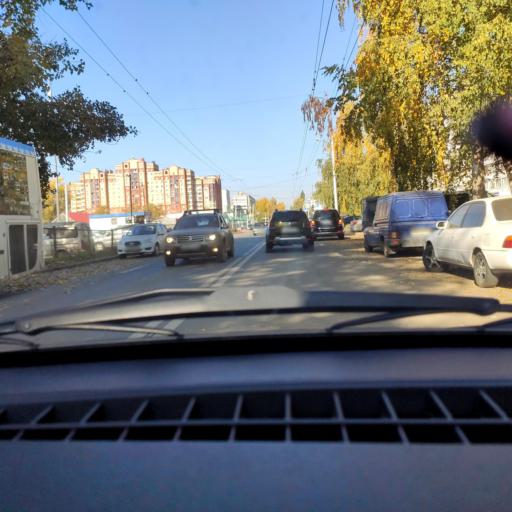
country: RU
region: Bashkortostan
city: Ufa
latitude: 54.7776
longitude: 56.1244
